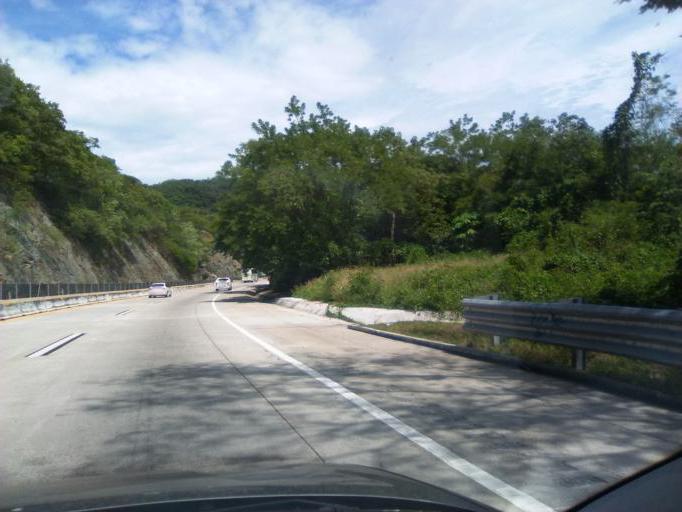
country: MX
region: Guerrero
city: Tierra Colorada
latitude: 17.1088
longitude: -99.5800
